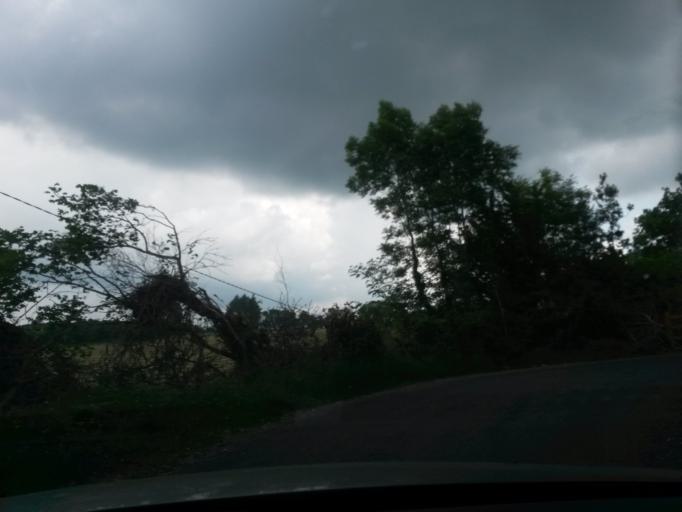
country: IE
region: Munster
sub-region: Ciarrai
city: Kenmare
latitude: 51.8650
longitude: -9.5686
